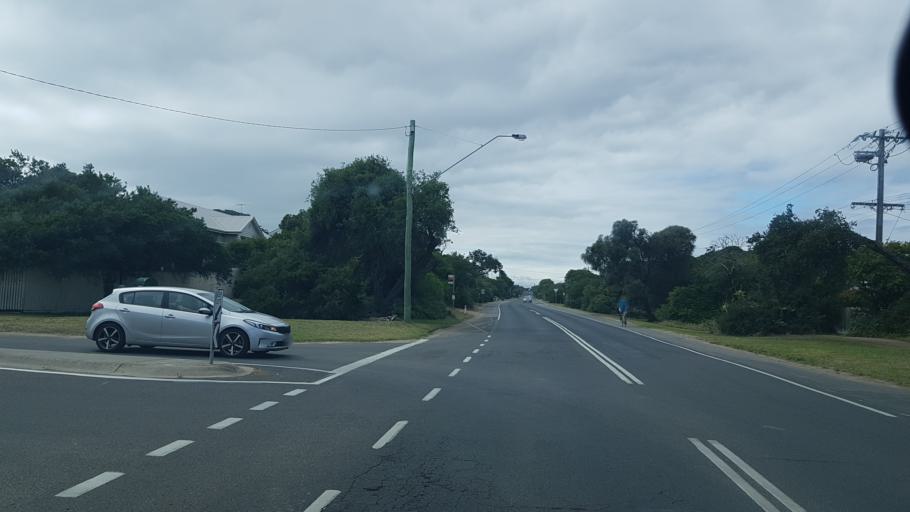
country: AU
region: Victoria
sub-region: Mornington Peninsula
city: Sorrento
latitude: -38.3478
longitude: 144.7422
